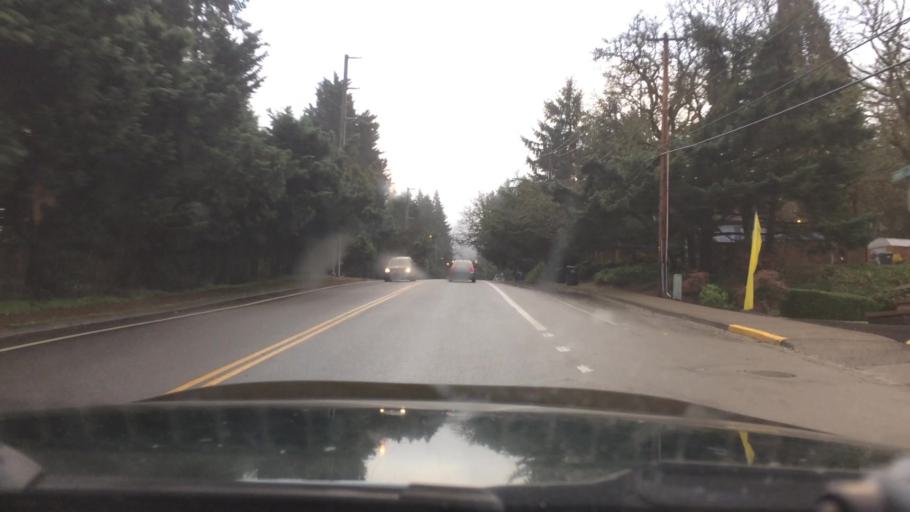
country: US
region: Oregon
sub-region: Lane County
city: Eugene
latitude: 44.0306
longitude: -123.1178
